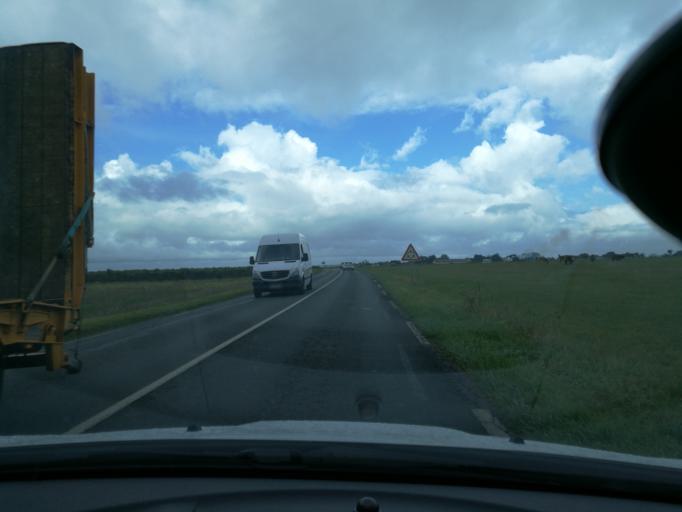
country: FR
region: Poitou-Charentes
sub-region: Departement de la Charente-Maritime
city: Saint-Martin-de-Re
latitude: 46.1977
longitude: -1.3683
